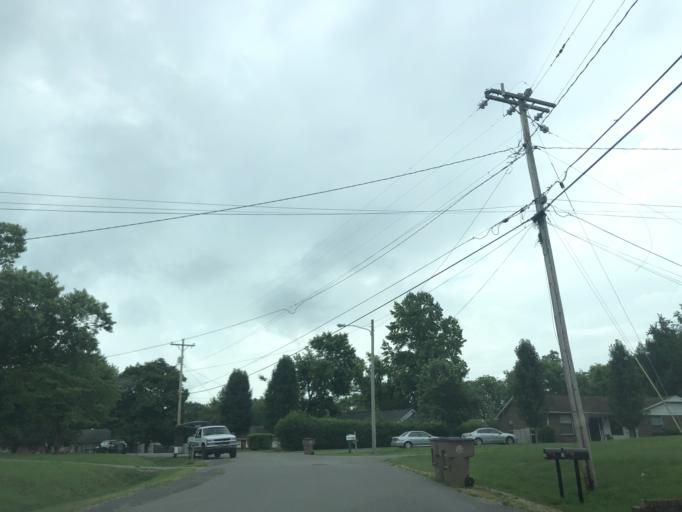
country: US
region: Tennessee
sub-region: Davidson County
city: Lakewood
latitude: 36.1586
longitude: -86.6700
